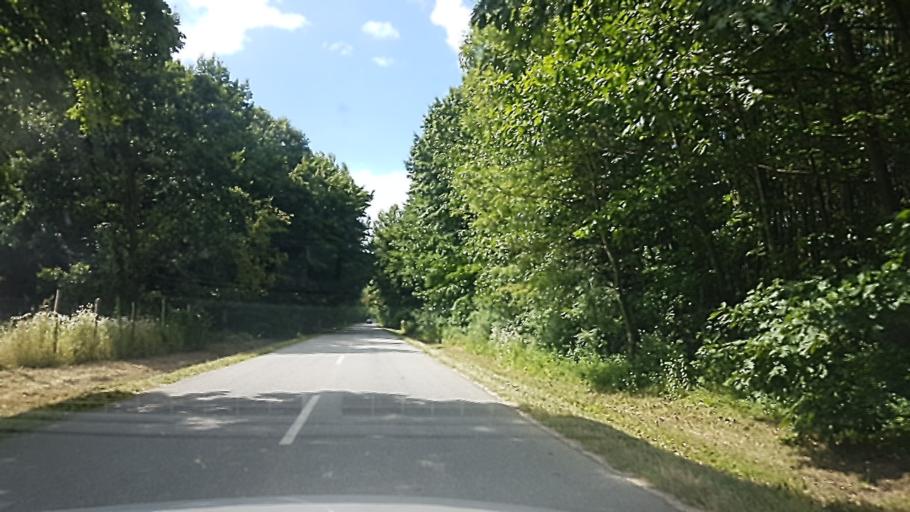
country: HU
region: Somogy
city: Barcs
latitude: 45.9409
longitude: 17.6376
